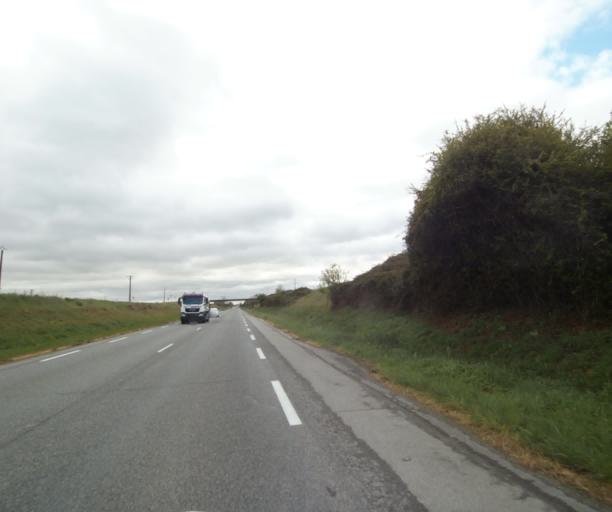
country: FR
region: Midi-Pyrenees
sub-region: Departement de l'Ariege
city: Saverdun
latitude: 43.2412
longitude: 1.5833
